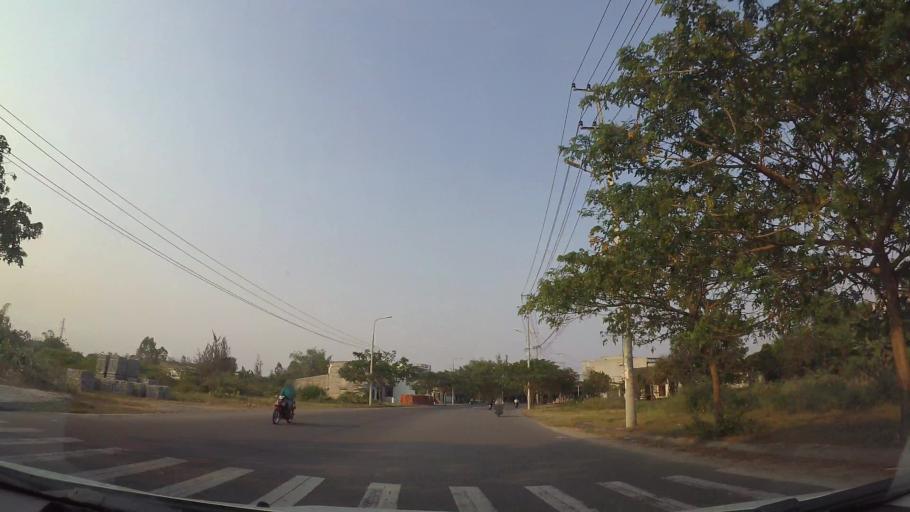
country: VN
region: Da Nang
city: Ngu Hanh Son
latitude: 15.9802
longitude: 108.2341
